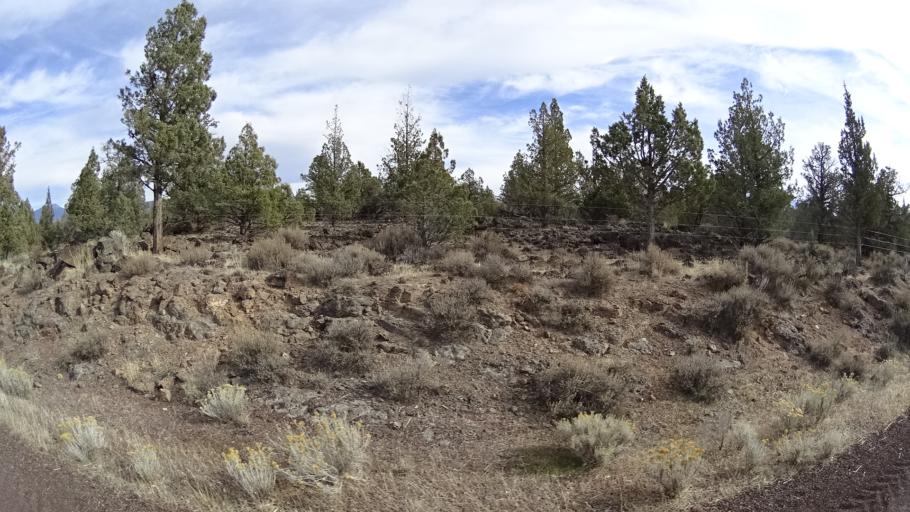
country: US
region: California
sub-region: Siskiyou County
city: Weed
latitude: 41.6015
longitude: -122.3952
